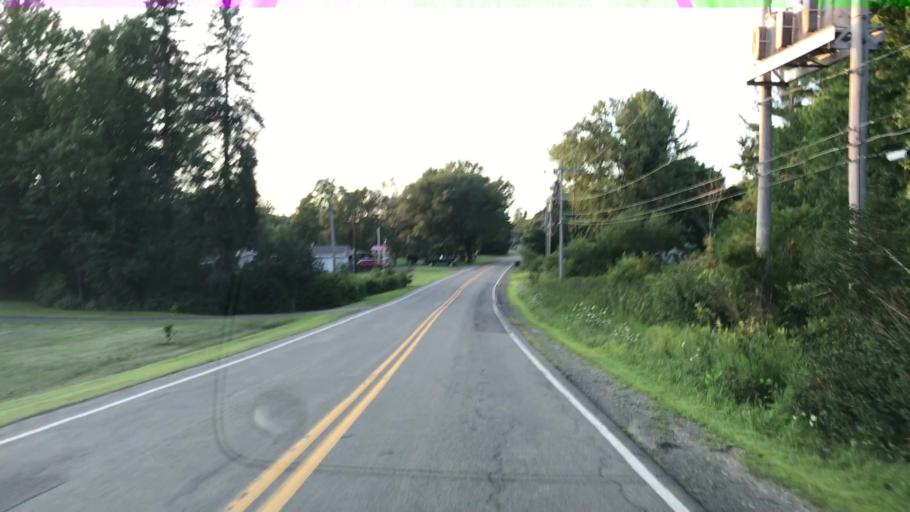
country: US
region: New York
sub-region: Chautauqua County
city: Mayville
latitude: 42.2623
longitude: -79.4703
